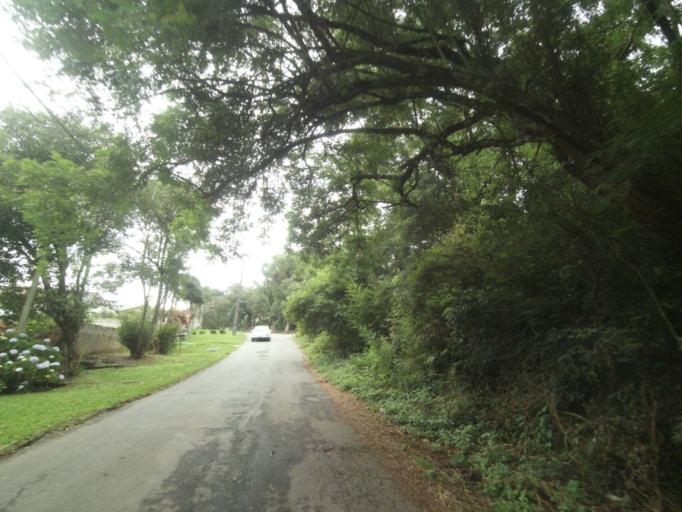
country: BR
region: Parana
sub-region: Curitiba
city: Curitiba
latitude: -25.4018
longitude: -49.2991
